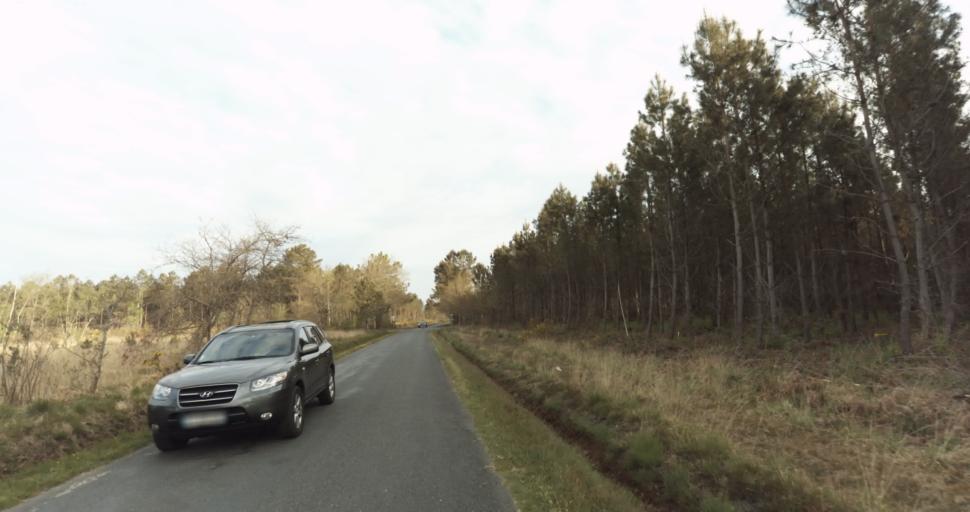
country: FR
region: Aquitaine
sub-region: Departement de la Gironde
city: Saint-Aubin-de-Medoc
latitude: 44.7899
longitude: -0.7566
